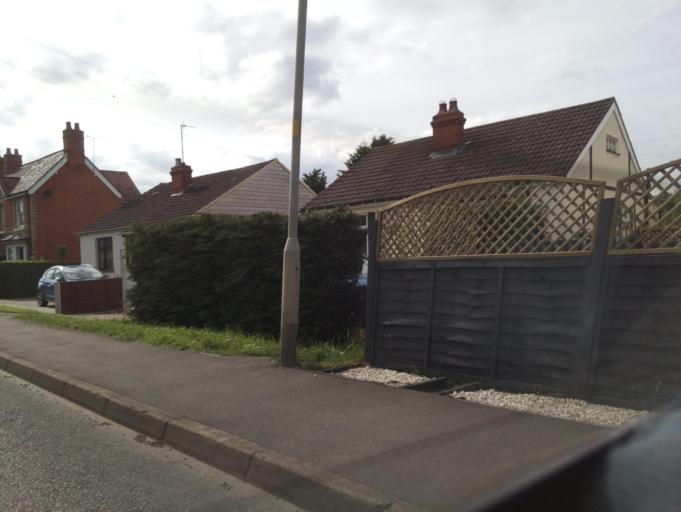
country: GB
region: England
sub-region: Worcestershire
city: Badsey
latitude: 52.0929
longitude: -1.8874
